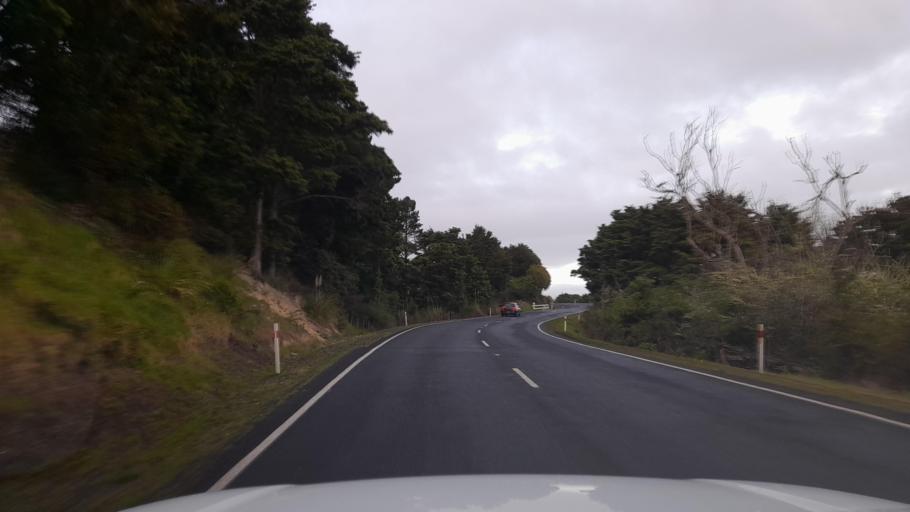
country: NZ
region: Northland
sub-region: Whangarei
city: Maungatapere
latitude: -35.7052
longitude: 174.0126
